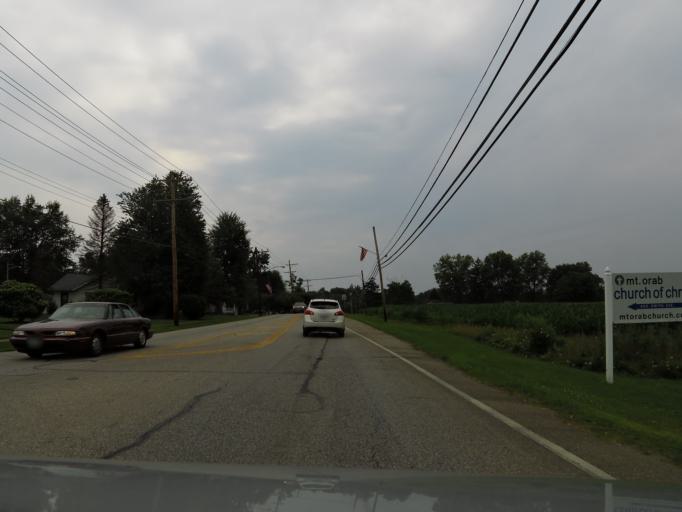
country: US
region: Ohio
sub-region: Brown County
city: Mount Orab
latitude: 39.0240
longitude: -83.9221
